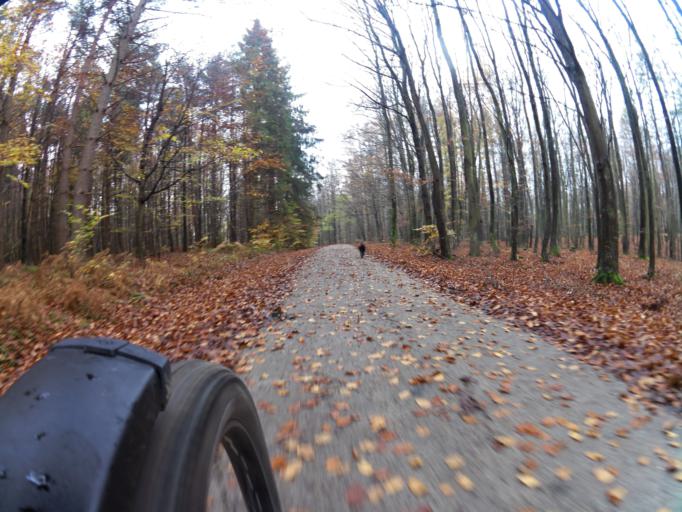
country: PL
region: Pomeranian Voivodeship
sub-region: Powiat pucki
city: Krokowa
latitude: 54.7700
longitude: 18.0929
